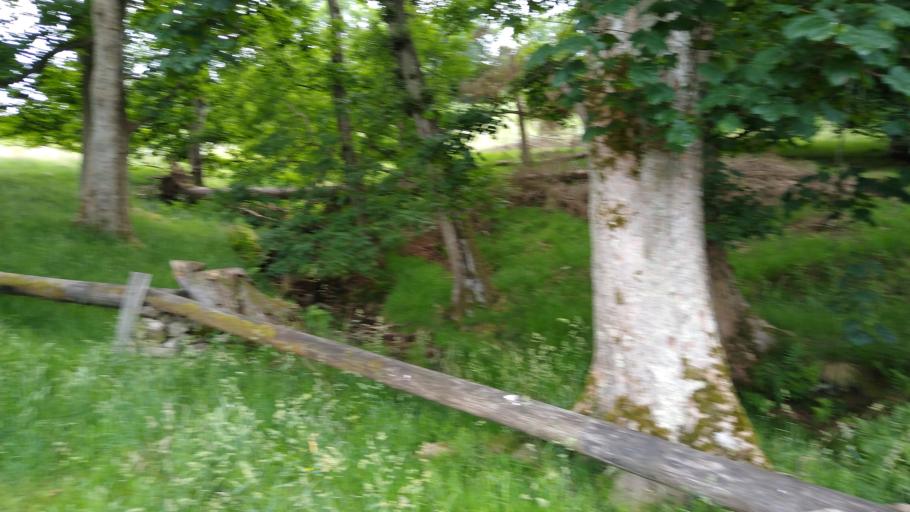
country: GB
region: England
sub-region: Northumberland
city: Greenhead
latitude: 54.9191
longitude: -2.6187
